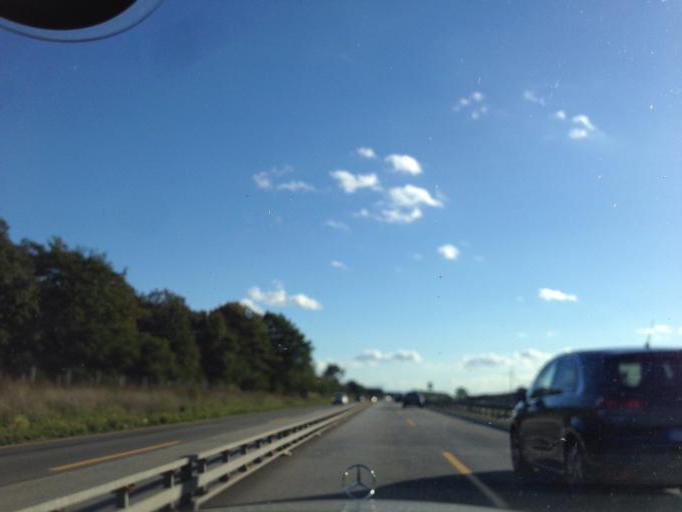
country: DE
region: Schleswig-Holstein
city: Loop
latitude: 54.1456
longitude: 9.9635
